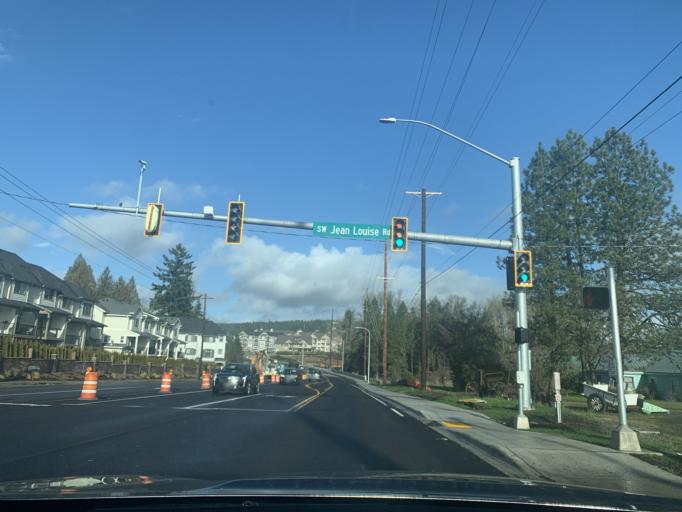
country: US
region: Oregon
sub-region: Washington County
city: King City
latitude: 45.4197
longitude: -122.8516
